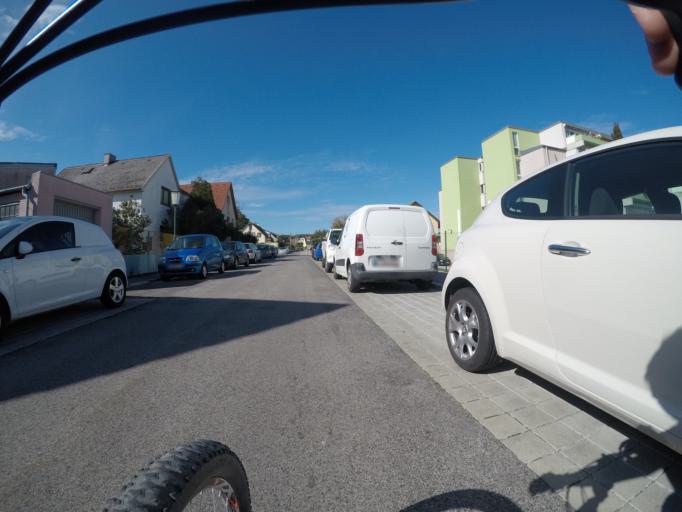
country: AT
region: Lower Austria
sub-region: Politischer Bezirk Modling
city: Brunn am Gebirge
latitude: 48.1055
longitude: 16.2917
